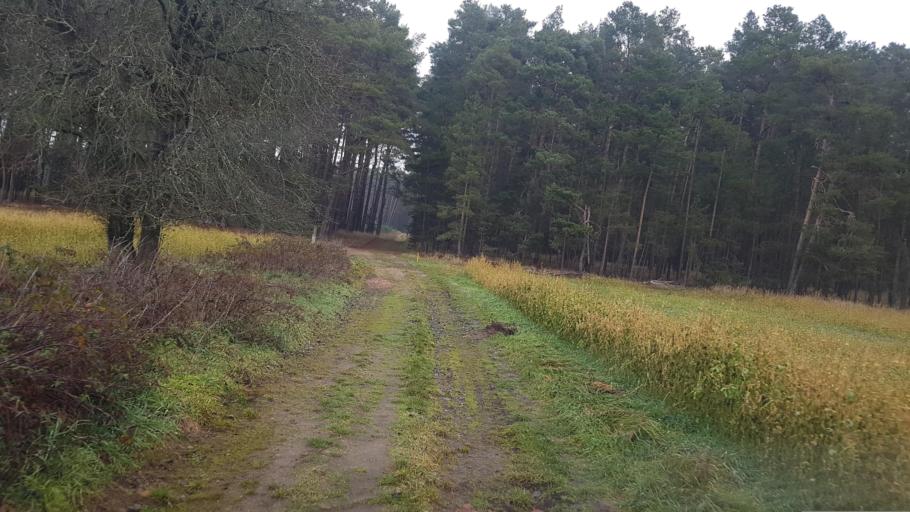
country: DE
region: Brandenburg
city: Sallgast
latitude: 51.6516
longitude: 13.8188
